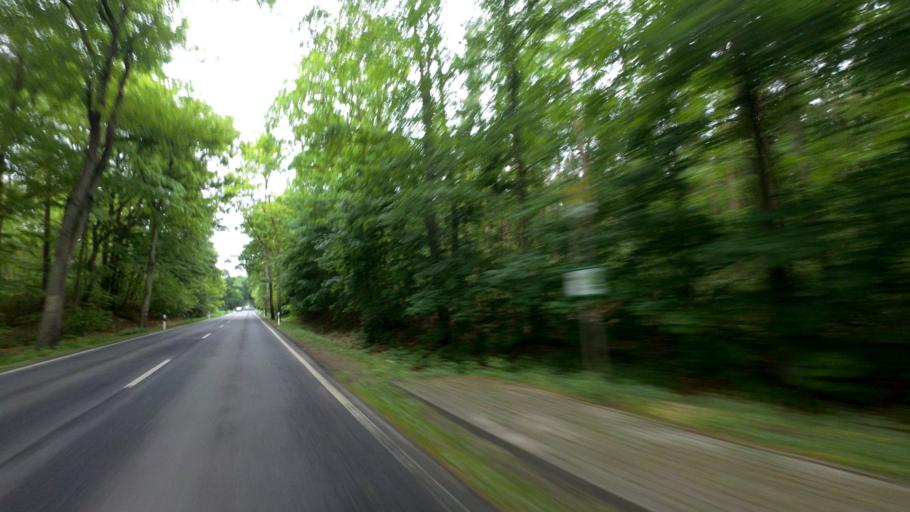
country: DE
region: Brandenburg
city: Marienwerder
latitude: 52.8677
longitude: 13.5368
